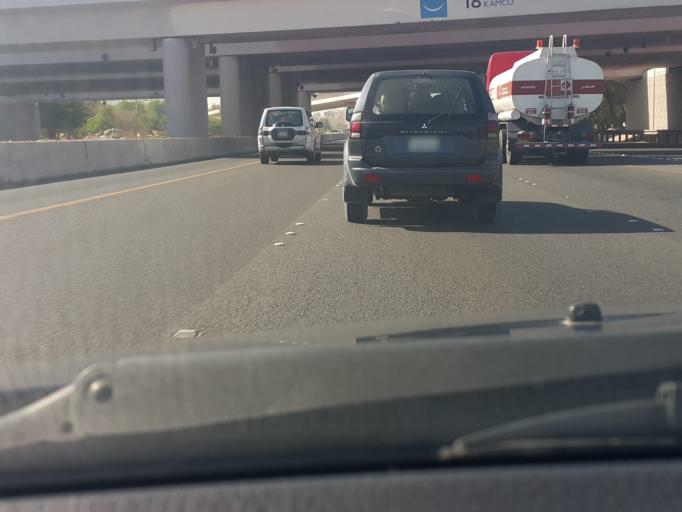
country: KW
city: Bayan
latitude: 29.3064
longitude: 48.0225
